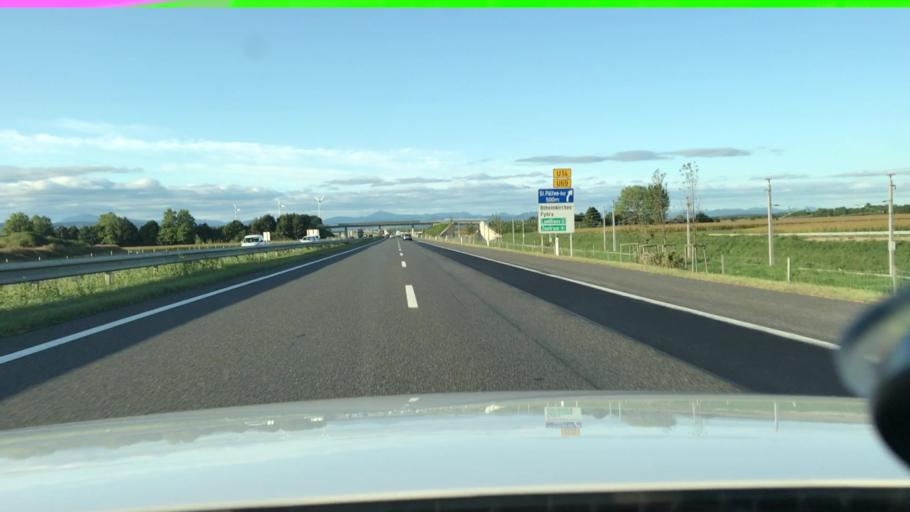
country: AT
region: Lower Austria
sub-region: Sankt Polten Stadt
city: Sankt Poelten
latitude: 48.2087
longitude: 15.6676
